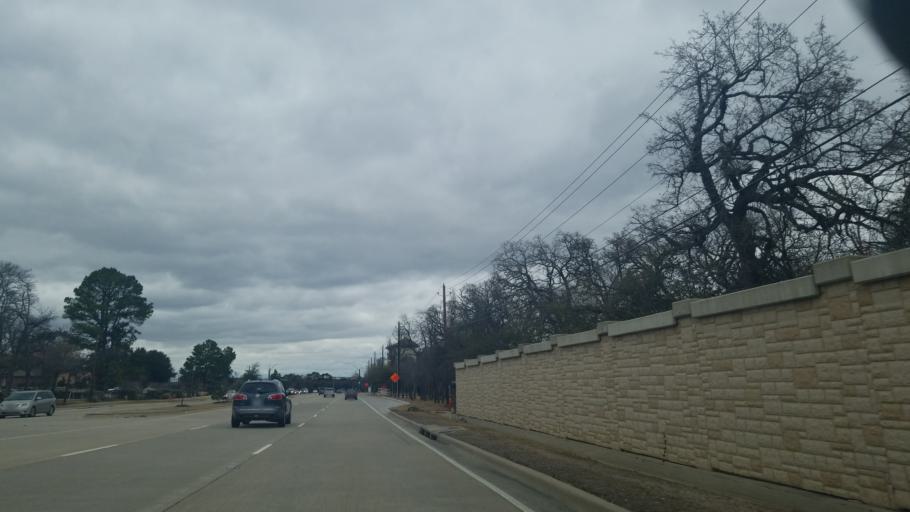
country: US
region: Texas
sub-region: Denton County
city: Flower Mound
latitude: 33.0413
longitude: -97.0694
